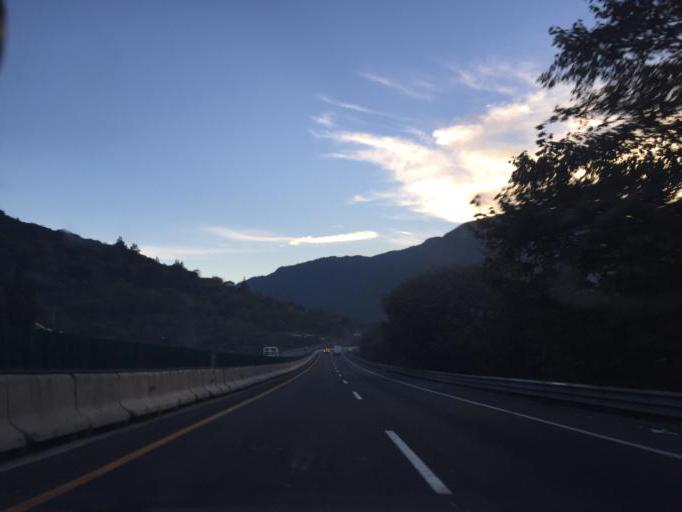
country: MX
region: Veracruz
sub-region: Nogales
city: Agricola Lazaro Cardenas
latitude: 18.8134
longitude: -97.1870
